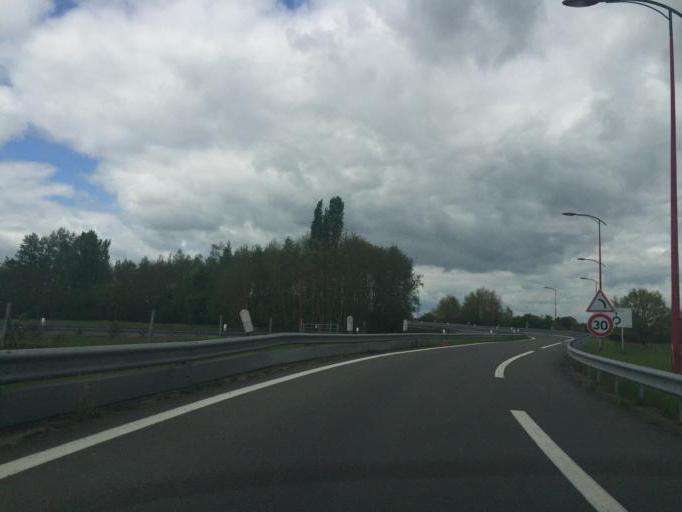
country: FR
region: Auvergne
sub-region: Departement de l'Allier
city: Avermes
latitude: 46.5975
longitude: 3.3101
